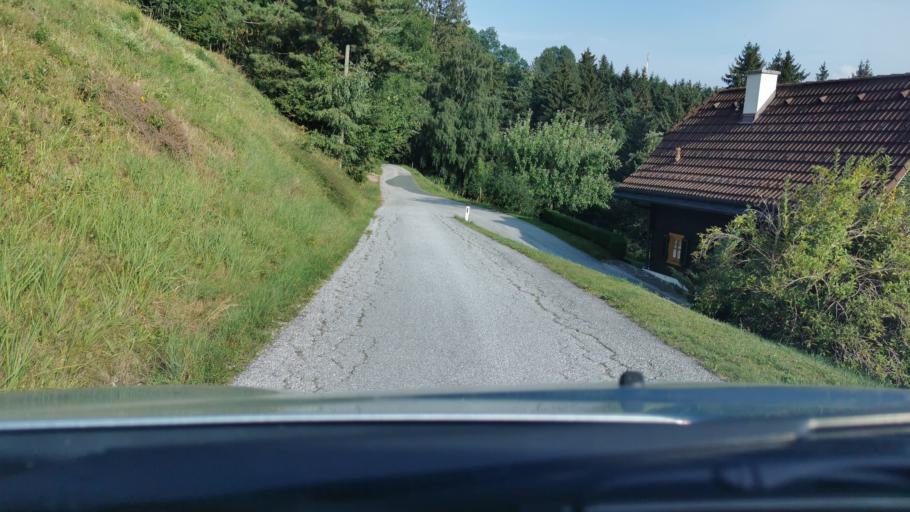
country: AT
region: Styria
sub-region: Politischer Bezirk Weiz
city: Fischbach
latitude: 47.3884
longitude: 15.6328
